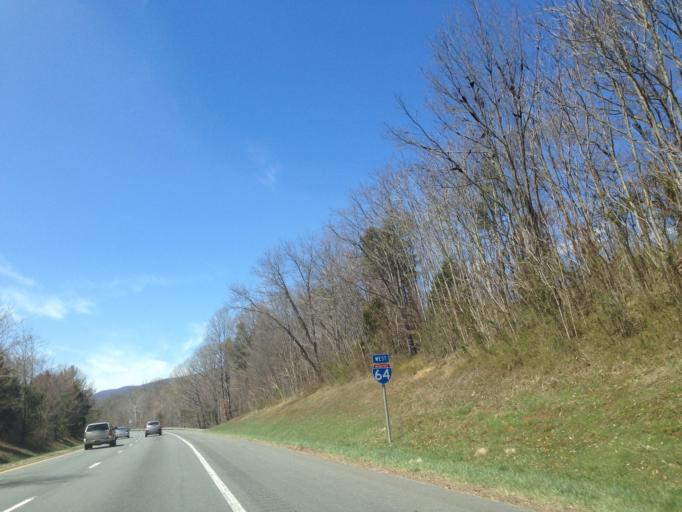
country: US
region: Virginia
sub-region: Albemarle County
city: Crozet
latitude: 38.0473
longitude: -78.7342
